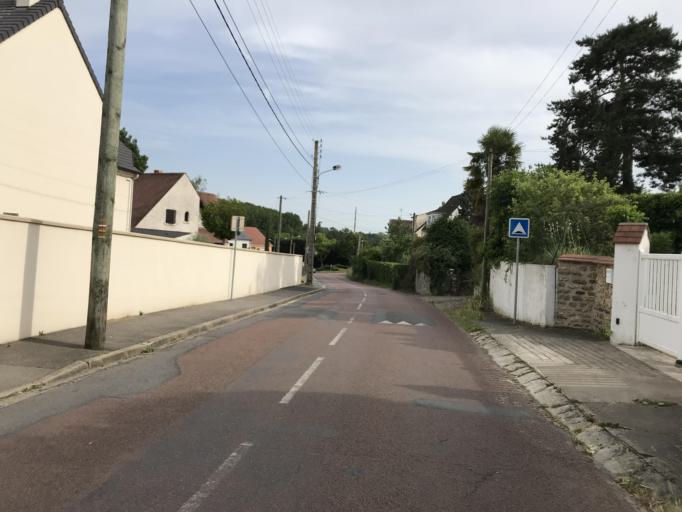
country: FR
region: Ile-de-France
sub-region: Departement de l'Essonne
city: Longpont-sur-Orge
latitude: 48.6279
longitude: 2.2907
